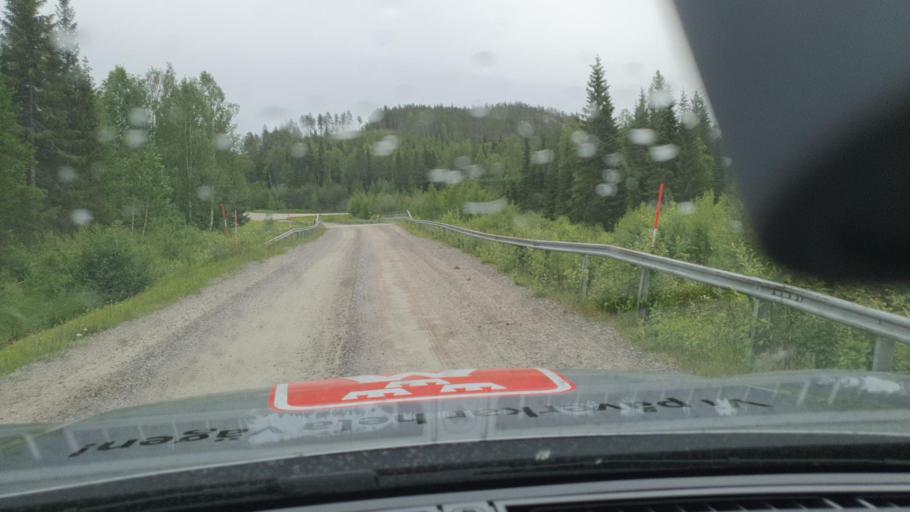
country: SE
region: Norrbotten
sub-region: Kalix Kommun
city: Rolfs
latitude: 66.0665
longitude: 23.0117
